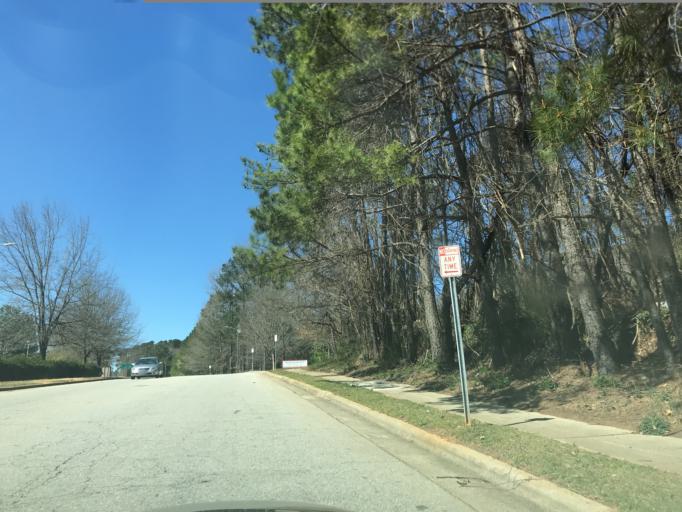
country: US
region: North Carolina
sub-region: Wake County
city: Raleigh
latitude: 35.7360
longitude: -78.6439
